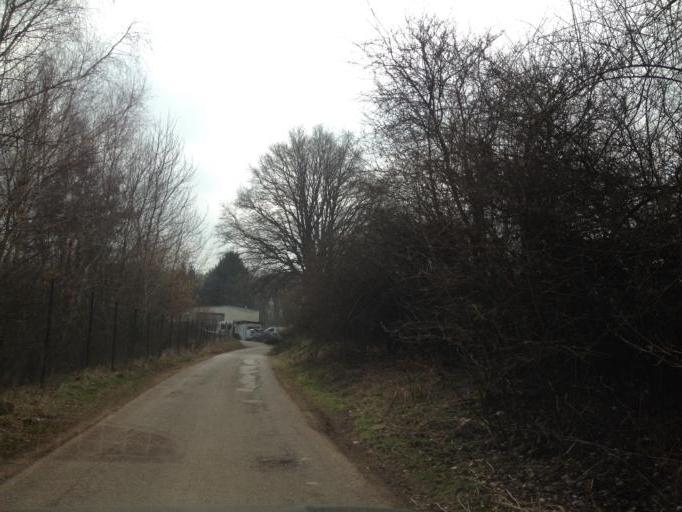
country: DE
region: Saarland
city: Sankt Wendel
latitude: 49.4657
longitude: 7.1373
